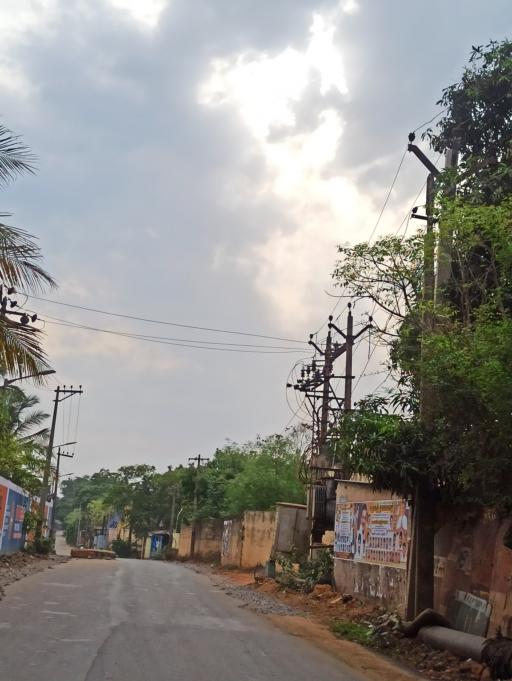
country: IN
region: Tamil Nadu
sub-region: Thiruvallur
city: Chinnasekkadu
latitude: 13.1683
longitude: 80.2344
